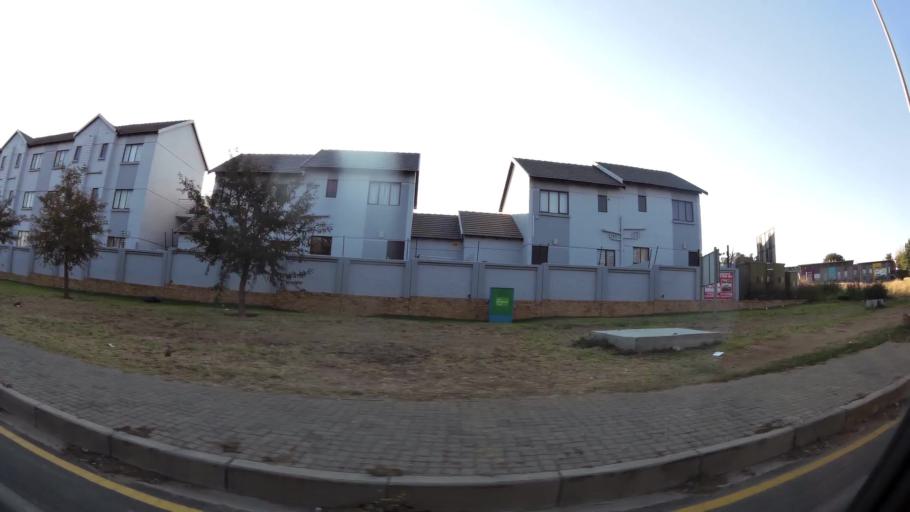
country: ZA
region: Gauteng
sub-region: City of Johannesburg Metropolitan Municipality
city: Midrand
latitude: -25.9936
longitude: 28.1189
